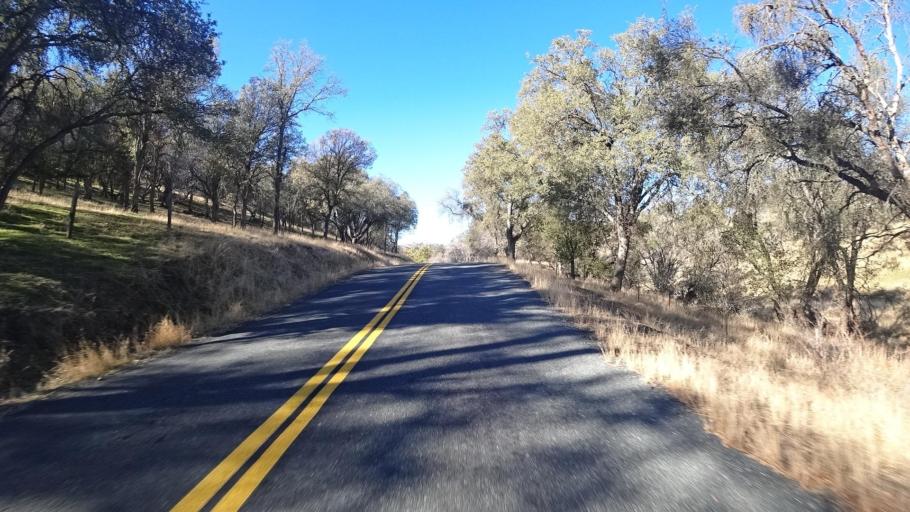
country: US
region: California
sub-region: Kern County
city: Alta Sierra
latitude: 35.7891
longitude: -118.7475
